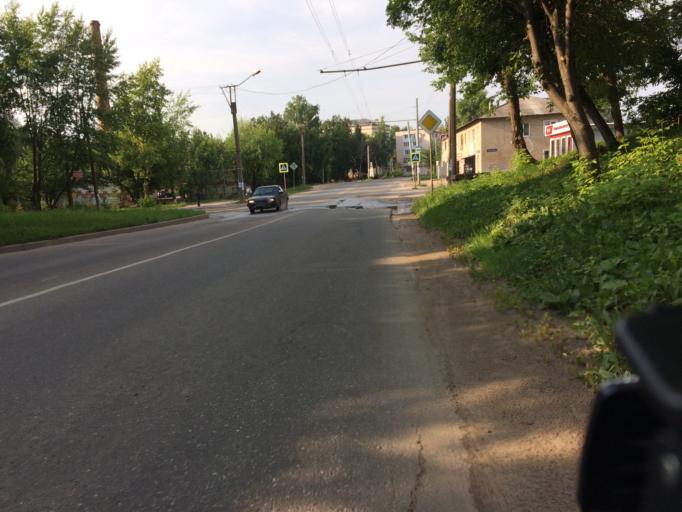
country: RU
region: Mariy-El
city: Yoshkar-Ola
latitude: 56.6283
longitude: 47.9471
